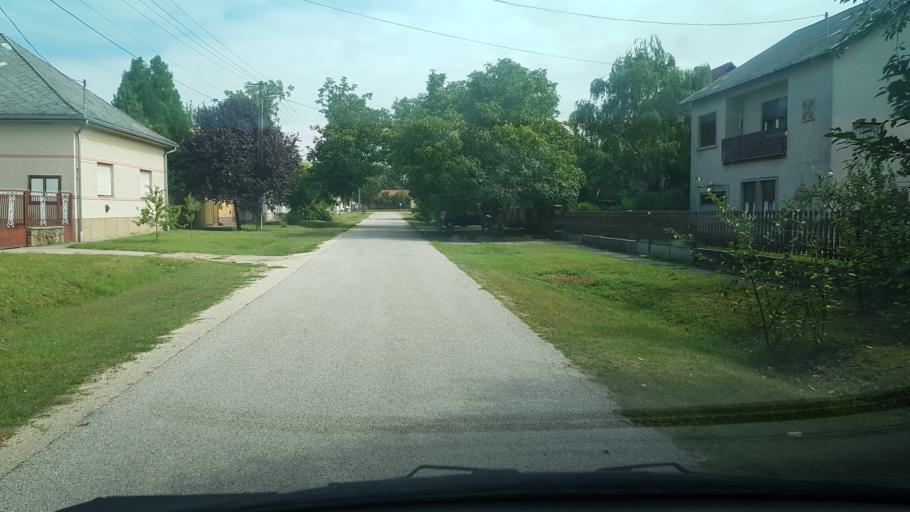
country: HU
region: Pest
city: Dunavarsany
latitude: 47.2867
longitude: 19.0345
